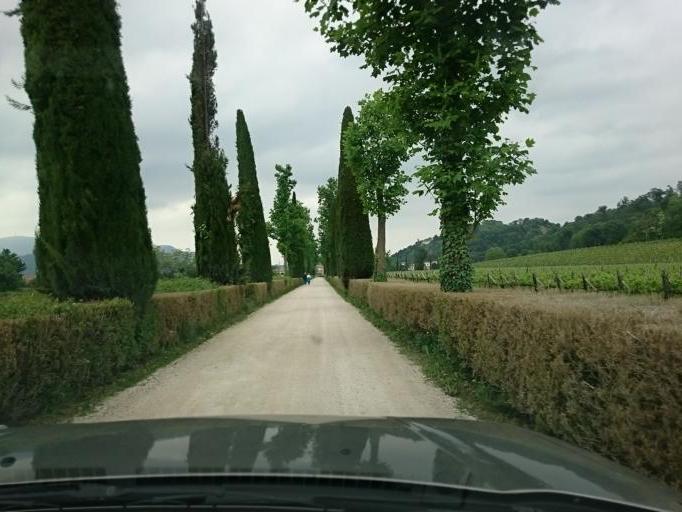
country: IT
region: Veneto
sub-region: Provincia di Padova
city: Battaglia Terme
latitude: 45.2744
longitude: 11.7657
